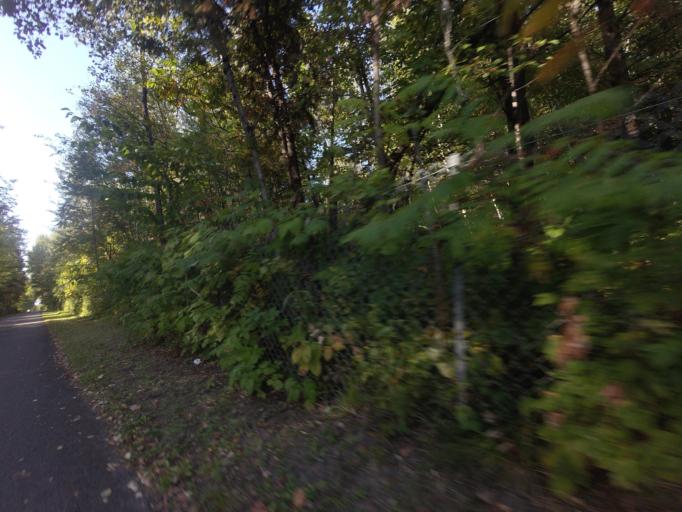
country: CA
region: Quebec
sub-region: Laurentides
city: Saint-Jerome
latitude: 45.7361
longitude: -73.9508
